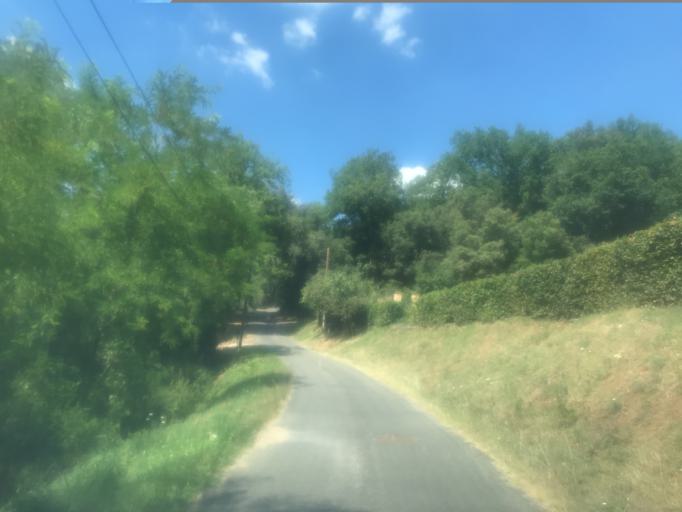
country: FR
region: Aquitaine
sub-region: Departement de la Dordogne
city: Cenac-et-Saint-Julien
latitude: 44.8245
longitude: 1.1931
